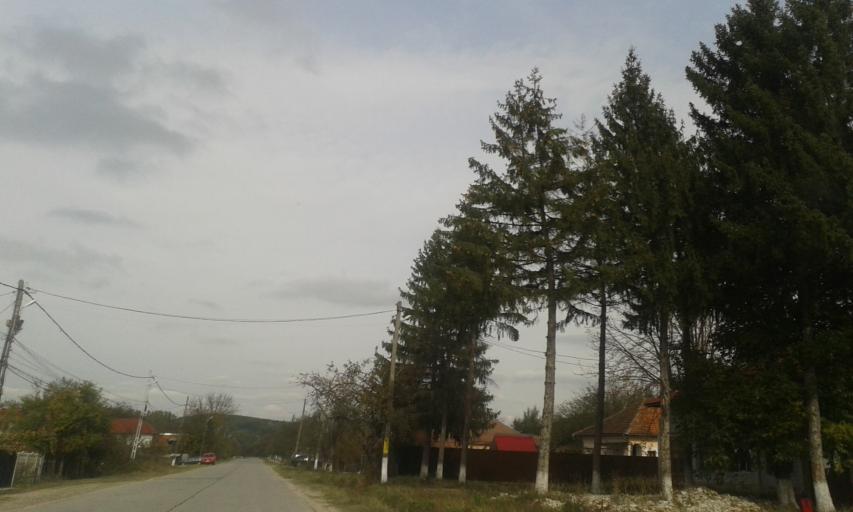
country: RO
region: Gorj
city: Logresti
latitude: 44.8769
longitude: 23.7090
